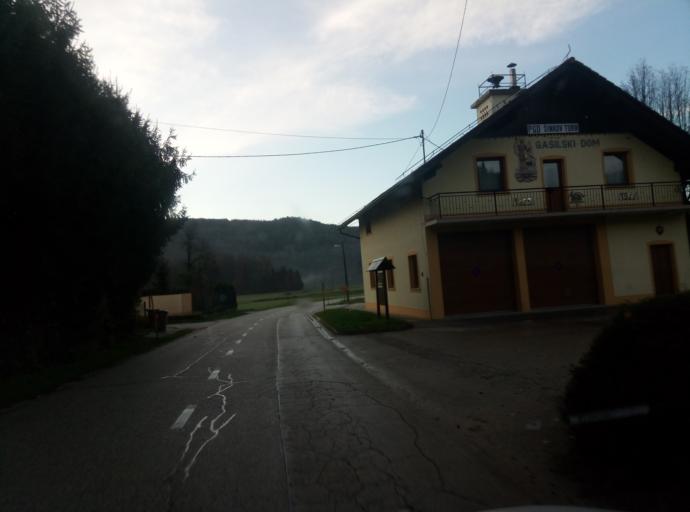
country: SI
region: Vodice
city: Vodice
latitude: 46.1683
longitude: 14.5190
